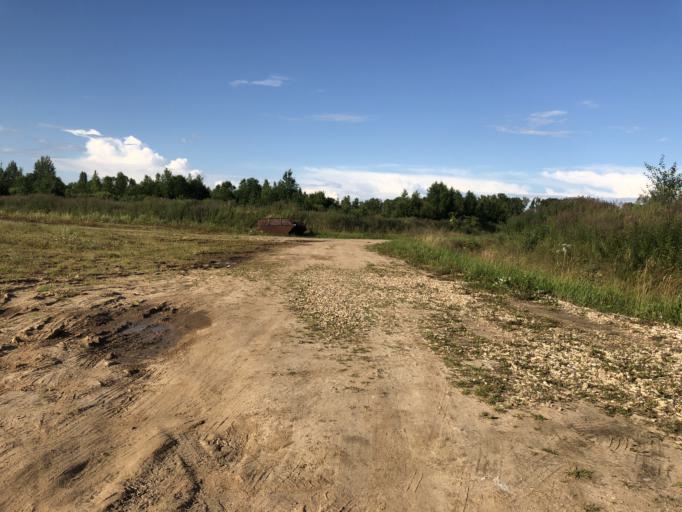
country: RU
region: Tverskaya
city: Rzhev
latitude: 56.2673
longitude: 34.2421
